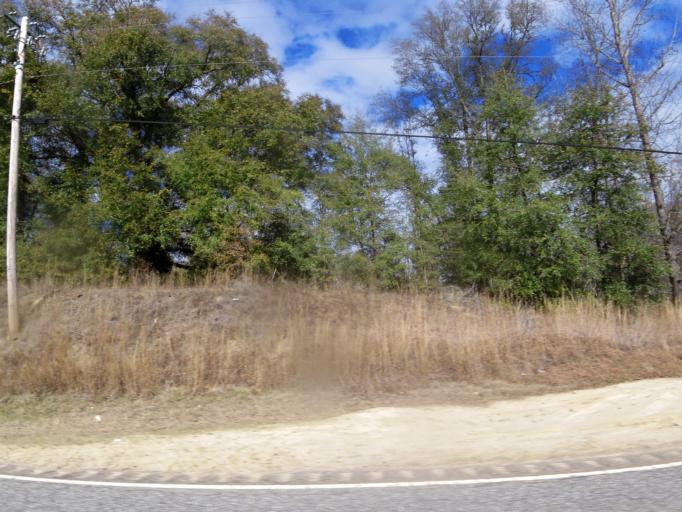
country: US
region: Alabama
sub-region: Barbour County
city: Eufaula
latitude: 32.0007
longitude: -85.2823
